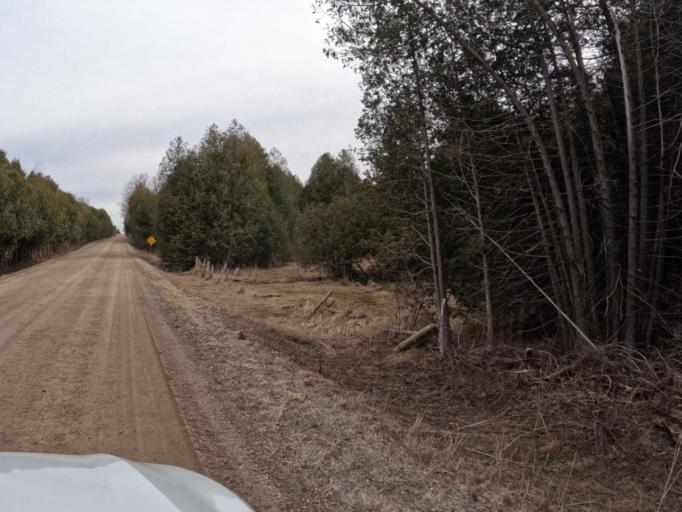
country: CA
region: Ontario
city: Shelburne
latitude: 43.9410
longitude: -80.2601
